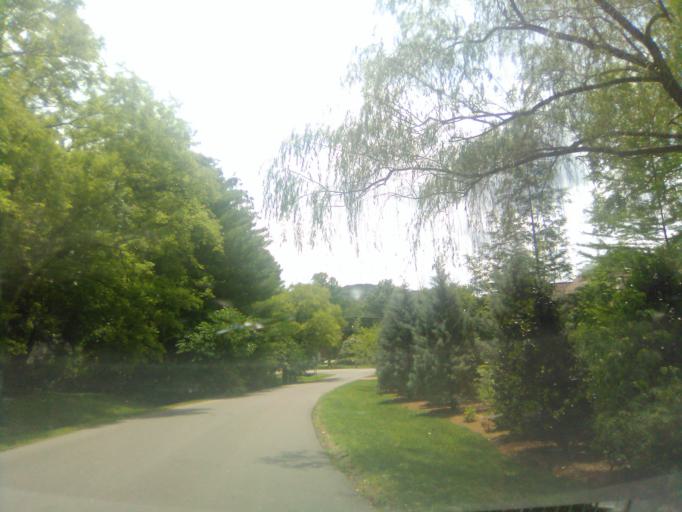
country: US
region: Tennessee
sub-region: Davidson County
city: Belle Meade
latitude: 36.0858
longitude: -86.8500
